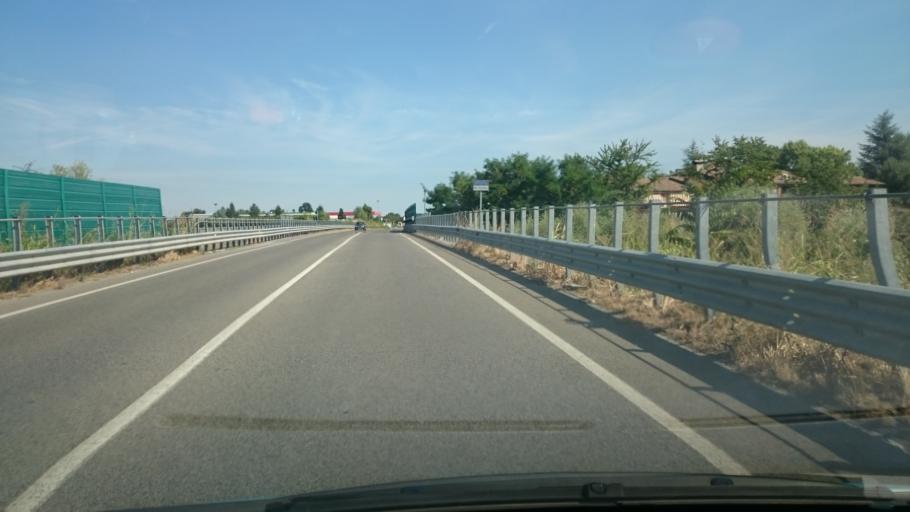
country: IT
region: Emilia-Romagna
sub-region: Provincia di Reggio Emilia
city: Scandiano
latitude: 44.5916
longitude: 10.7135
